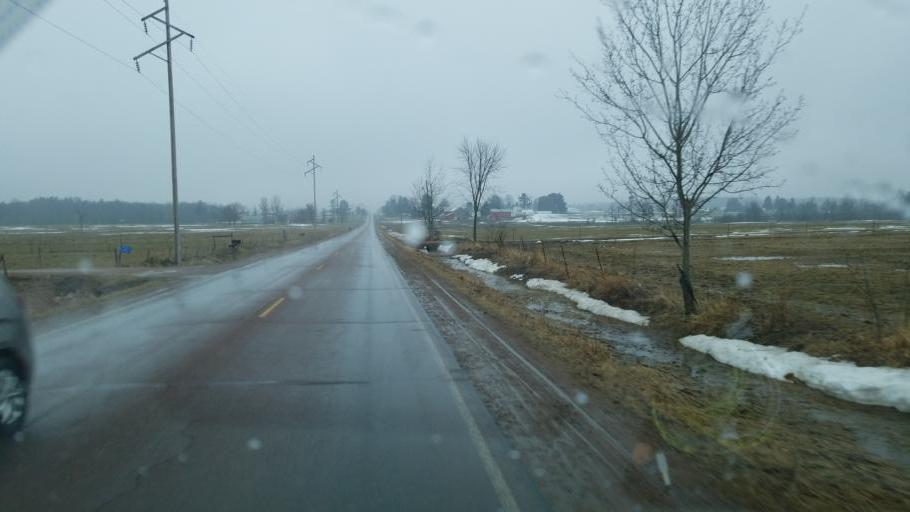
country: US
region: Wisconsin
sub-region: Clark County
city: Loyal
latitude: 44.5751
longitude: -90.3958
